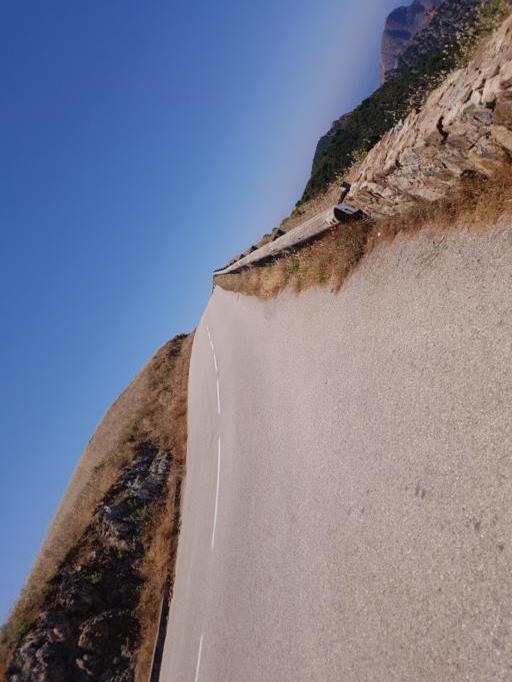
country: FR
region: Corsica
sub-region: Departement de la Corse-du-Sud
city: Cargese
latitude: 42.2426
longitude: 8.6007
